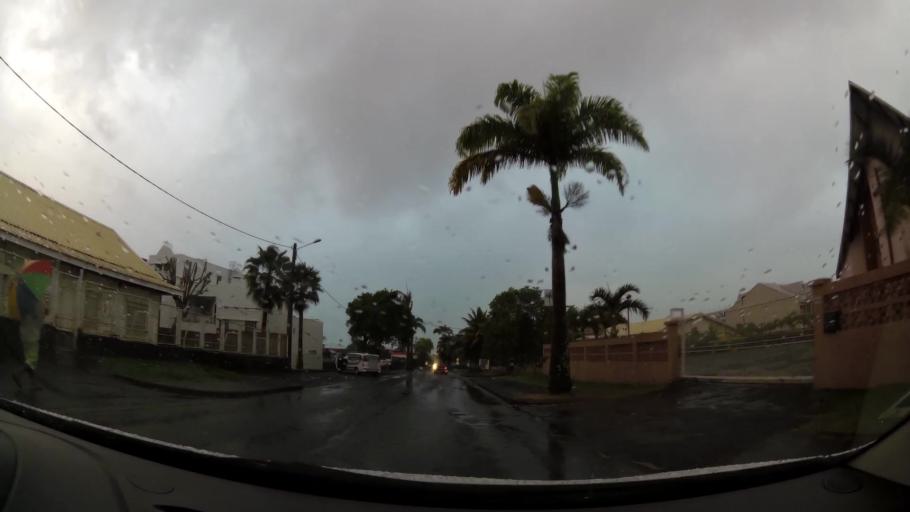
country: RE
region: Reunion
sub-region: Reunion
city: Saint-Benoit
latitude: -21.0437
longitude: 55.7209
